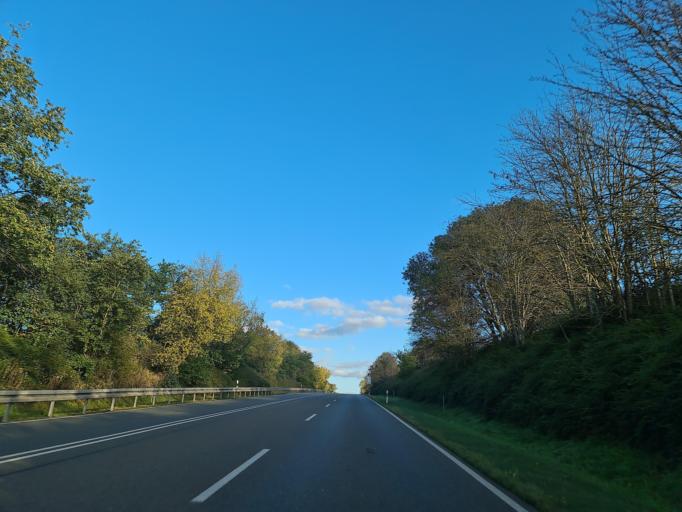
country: DE
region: Thuringia
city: Weida
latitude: 50.7715
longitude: 12.0741
